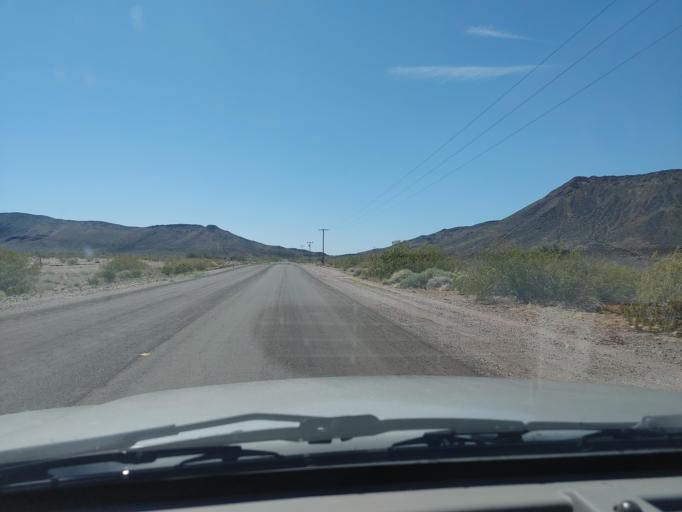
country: US
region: Arizona
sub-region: Maricopa County
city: Gila Bend
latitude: 33.0167
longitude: -113.3404
